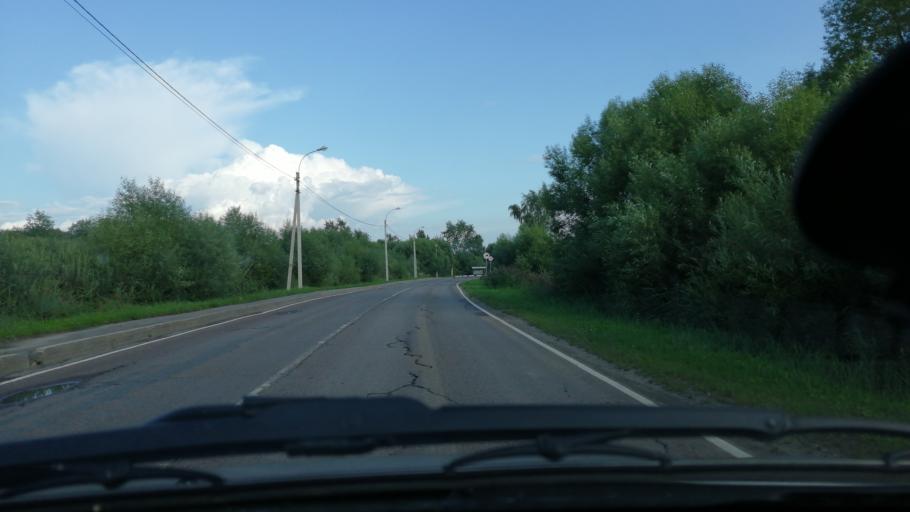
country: RU
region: Moskovskaya
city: Troitskoye
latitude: 55.2851
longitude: 38.5399
